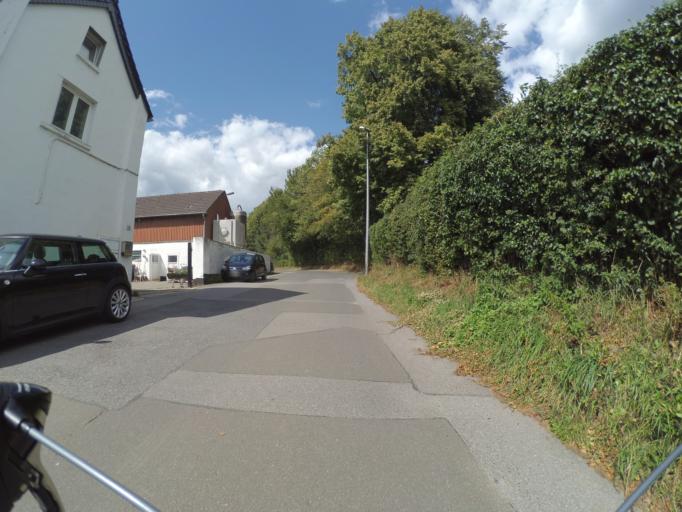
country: DE
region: North Rhine-Westphalia
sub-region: Regierungsbezirk Koln
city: Aachen
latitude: 50.8027
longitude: 6.0928
